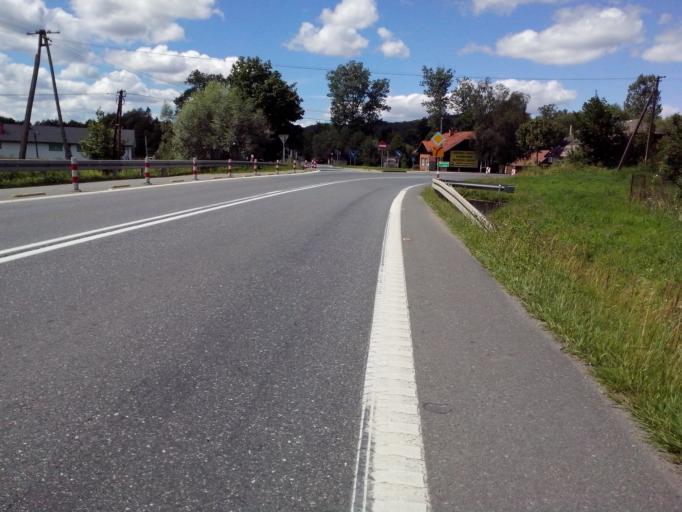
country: PL
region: Subcarpathian Voivodeship
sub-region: Powiat strzyzowski
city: Jawornik
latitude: 49.8070
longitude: 21.8864
